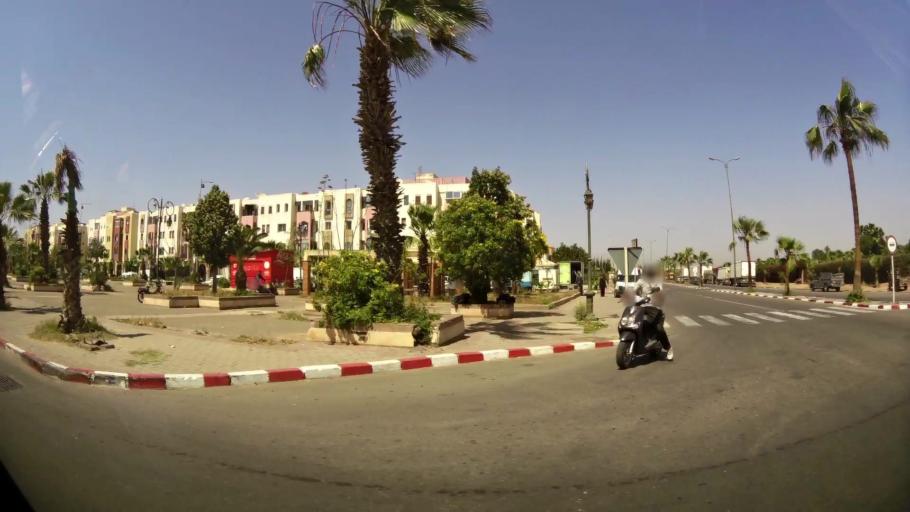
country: MA
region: Souss-Massa-Draa
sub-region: Inezgane-Ait Mellou
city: Inezgane
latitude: 30.3603
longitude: -9.5256
